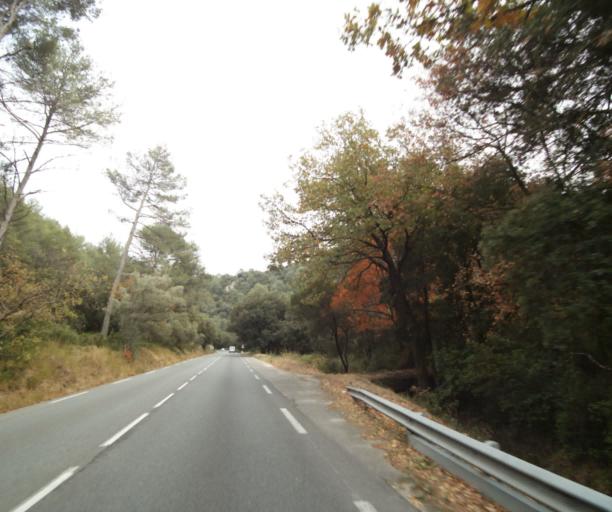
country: FR
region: Provence-Alpes-Cote d'Azur
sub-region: Departement des Bouches-du-Rhone
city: Gemenos
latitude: 43.2673
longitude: 5.6508
